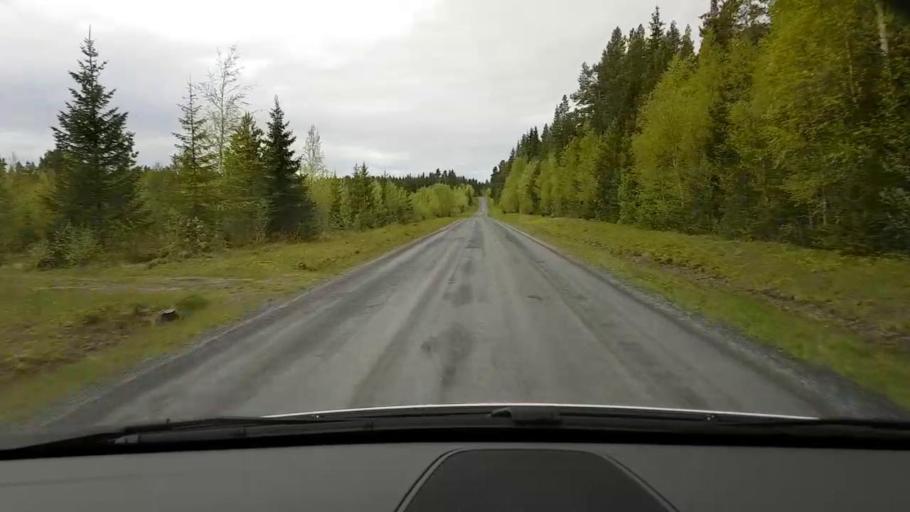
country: SE
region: Jaemtland
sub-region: Krokoms Kommun
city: Valla
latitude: 63.3069
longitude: 13.9966
